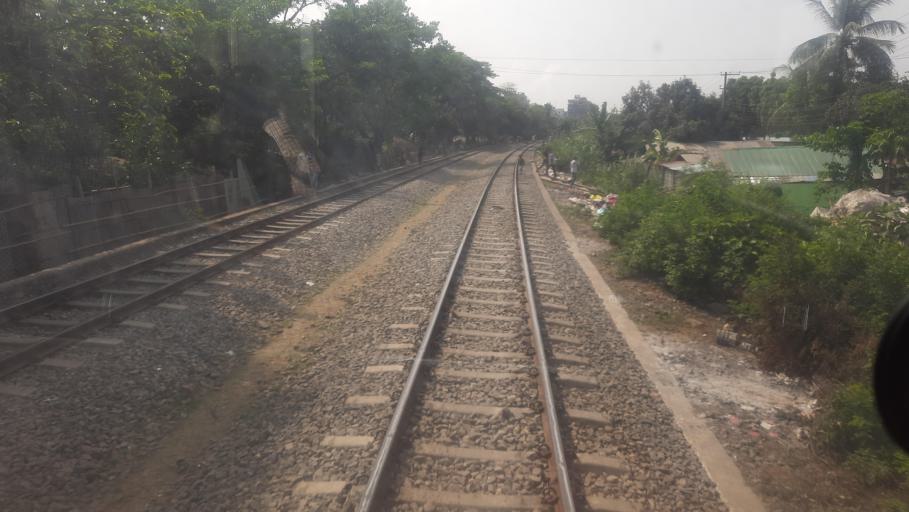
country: BD
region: Chittagong
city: Chittagong
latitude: 22.3591
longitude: 91.7889
